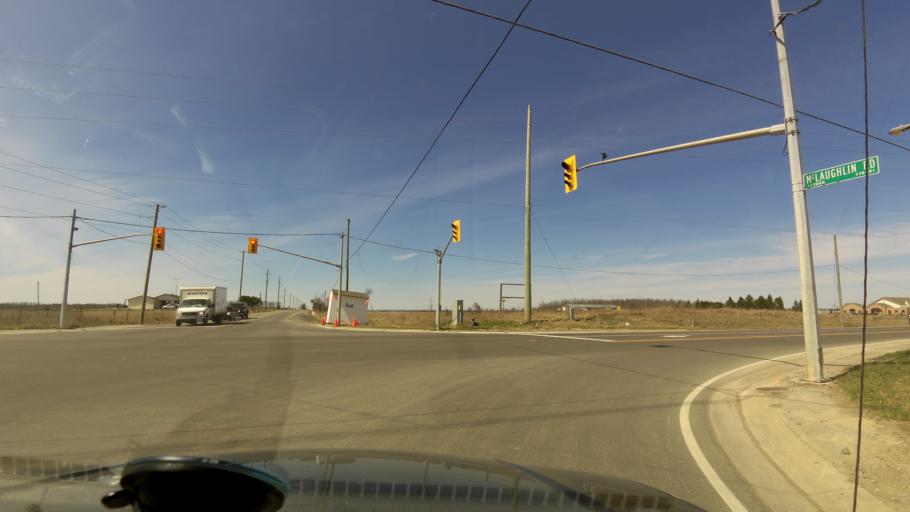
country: CA
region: Ontario
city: Brampton
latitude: 43.7238
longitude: -79.8352
